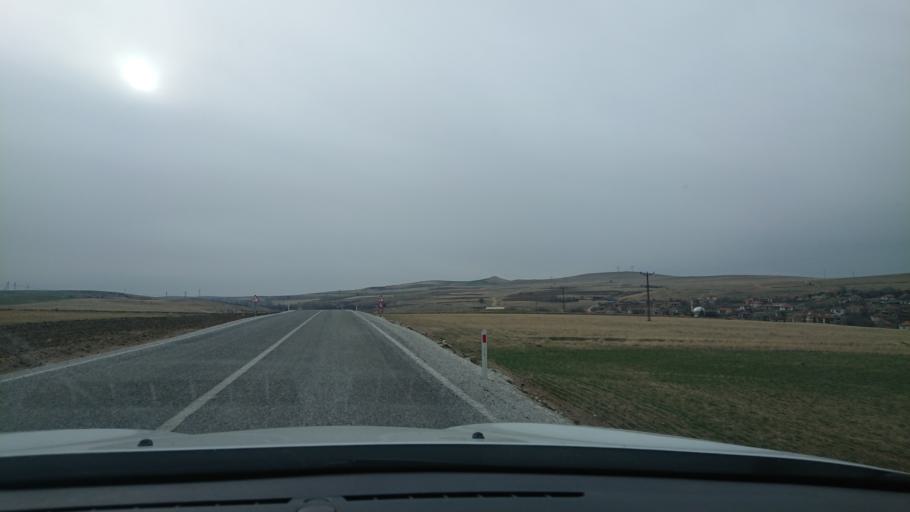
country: TR
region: Aksaray
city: Agacoren
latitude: 38.9212
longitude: 33.9345
